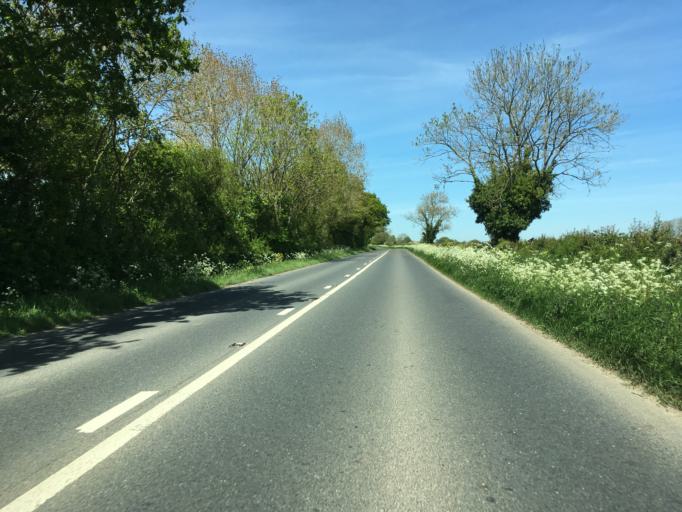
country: GB
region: England
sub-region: Wiltshire
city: Hankerton
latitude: 51.6410
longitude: -2.0614
